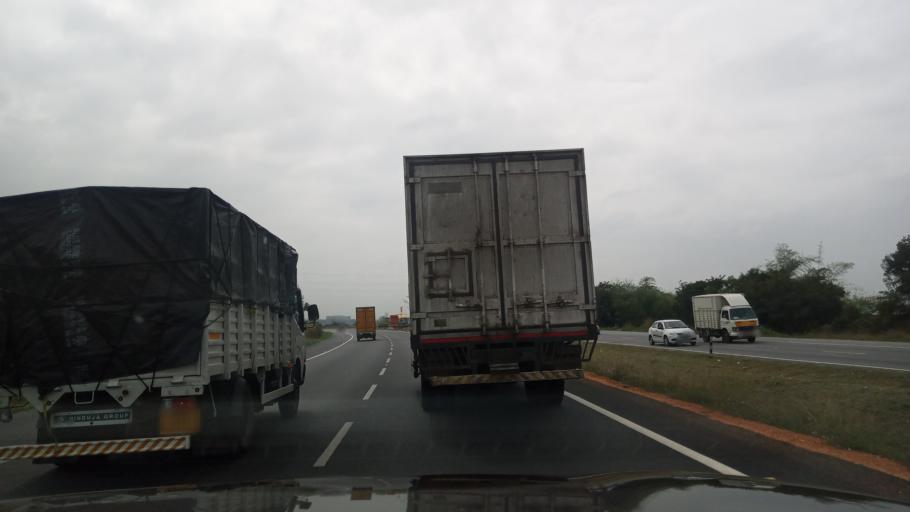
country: IN
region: Karnataka
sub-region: Bangalore Urban
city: Bangalore
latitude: 12.9143
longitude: 77.4676
